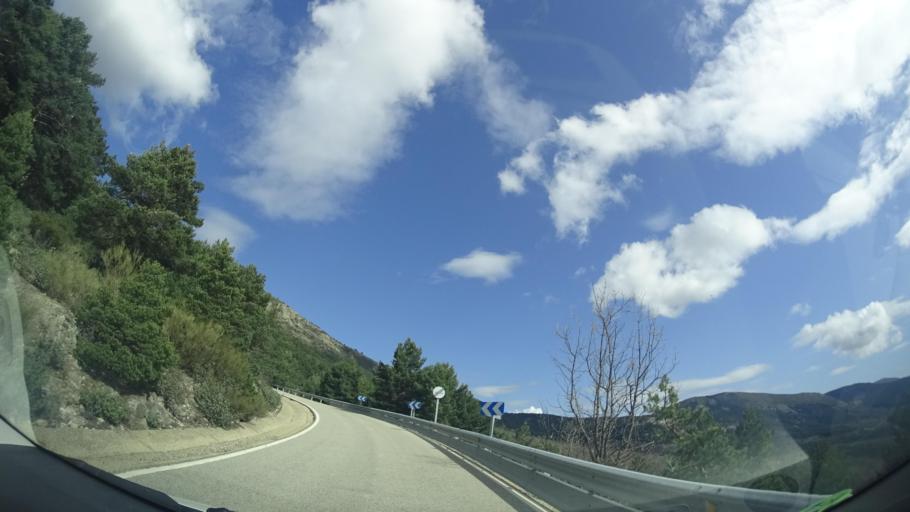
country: ES
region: Madrid
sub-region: Provincia de Madrid
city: Miraflores de la Sierra
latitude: 40.8465
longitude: -3.7646
